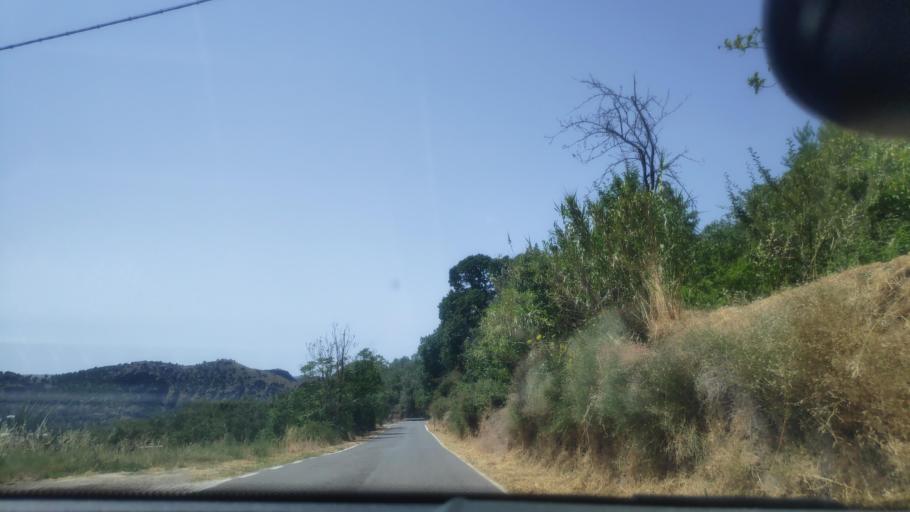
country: ES
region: Andalusia
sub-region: Provincia de Granada
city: Busquistar
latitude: 36.9599
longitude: -3.2784
